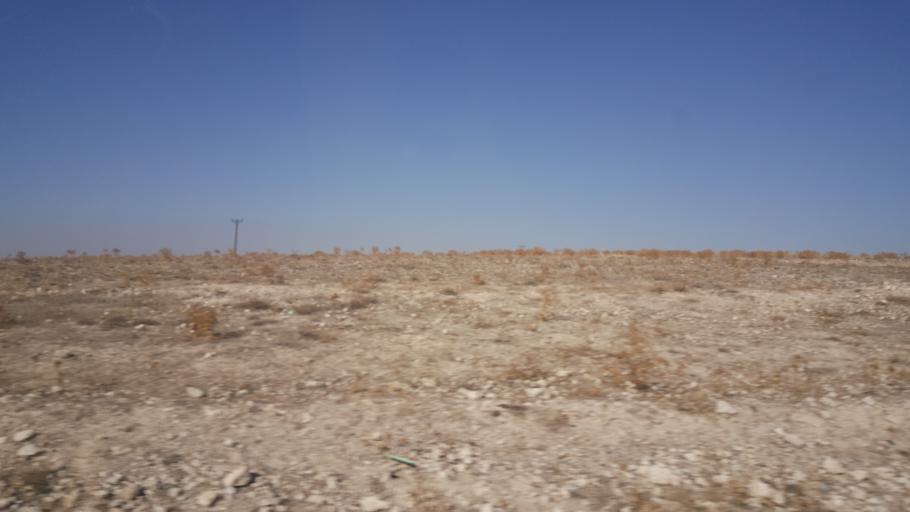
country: TR
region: Konya
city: Celtik
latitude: 39.0614
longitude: 31.8621
